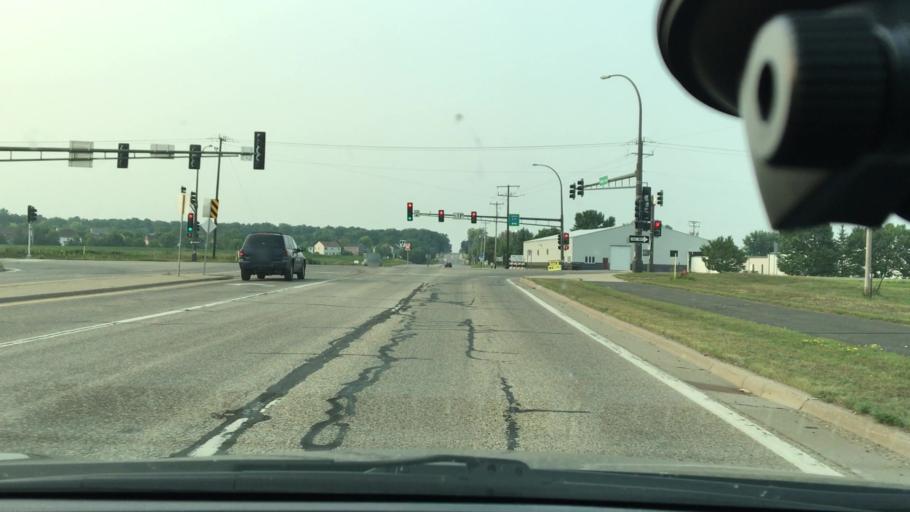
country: US
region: Minnesota
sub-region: Wright County
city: Albertville
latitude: 45.2119
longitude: -93.6240
